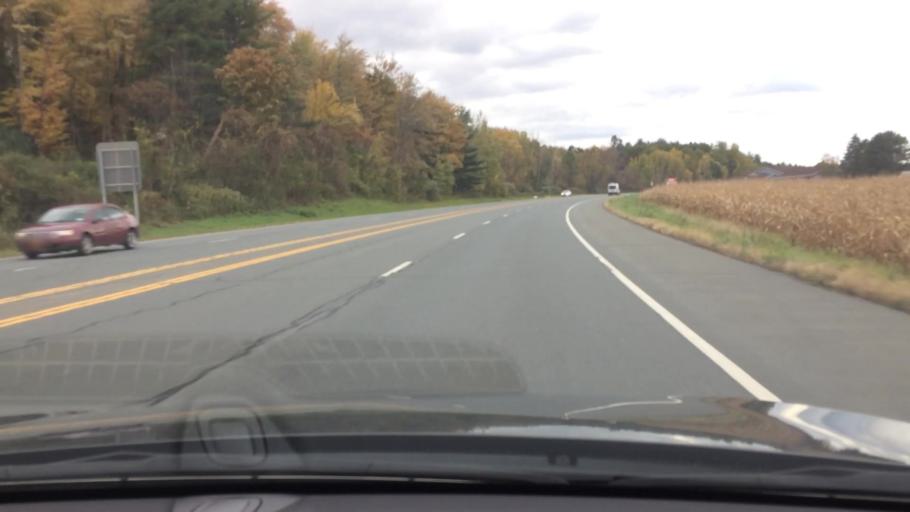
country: US
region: New York
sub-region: Columbia County
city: Niverville
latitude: 42.4807
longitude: -73.6799
